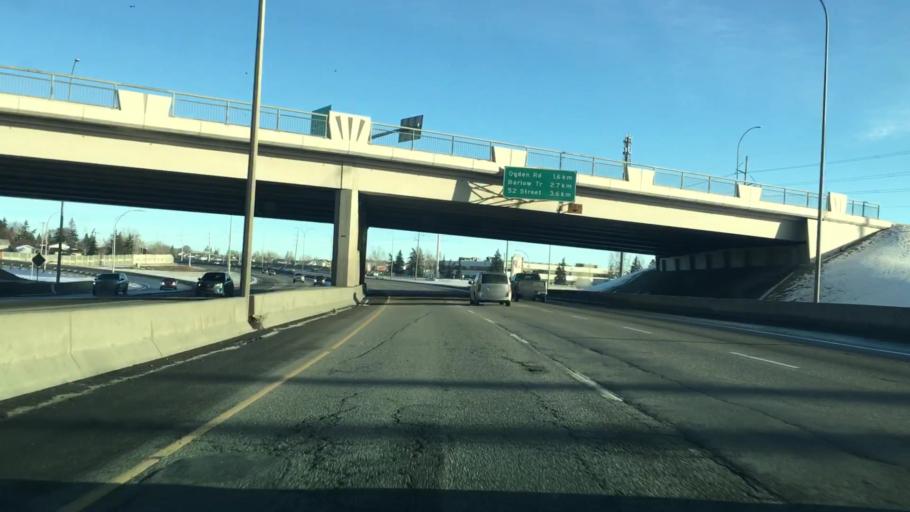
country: CA
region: Alberta
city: Calgary
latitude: 50.9808
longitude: -114.0165
